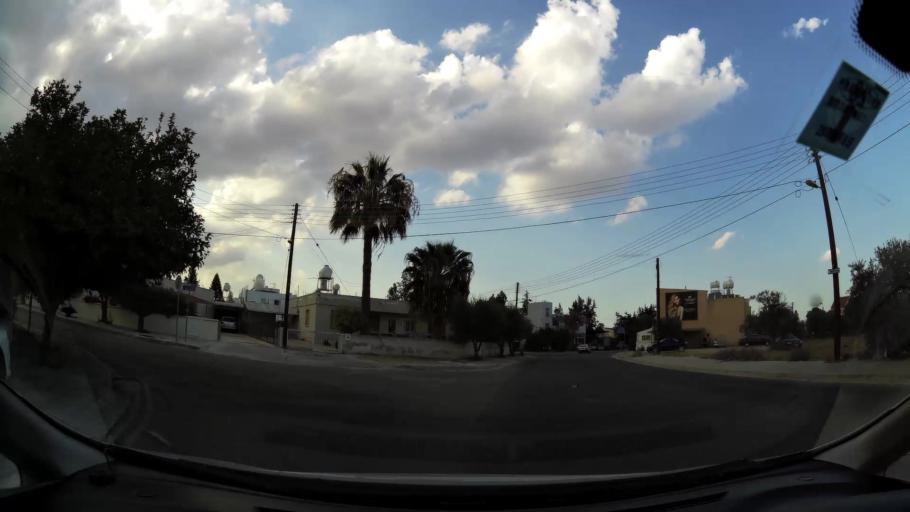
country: CY
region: Lefkosia
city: Kato Deftera
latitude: 35.1098
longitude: 33.3018
